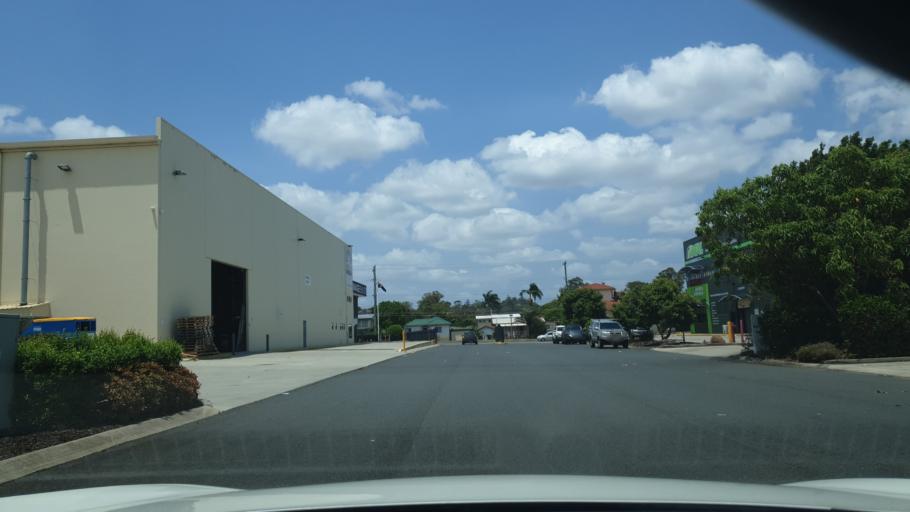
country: AU
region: Queensland
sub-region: Brisbane
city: Zillmere
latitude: -27.3566
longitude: 153.0275
